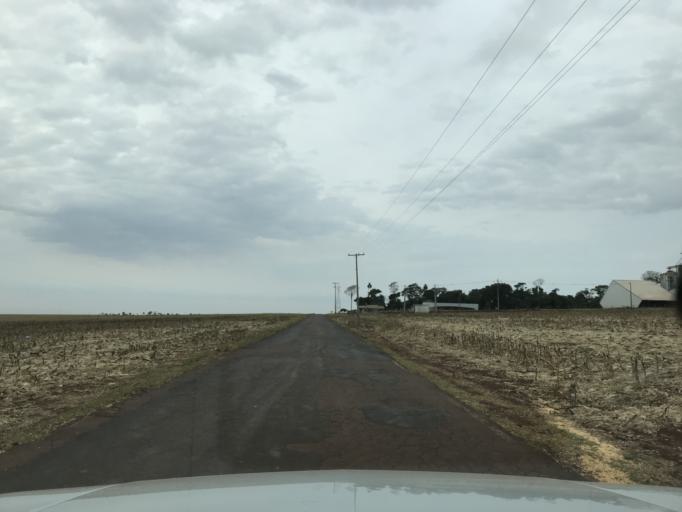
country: BR
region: Parana
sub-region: Palotina
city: Palotina
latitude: -24.2848
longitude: -53.7941
